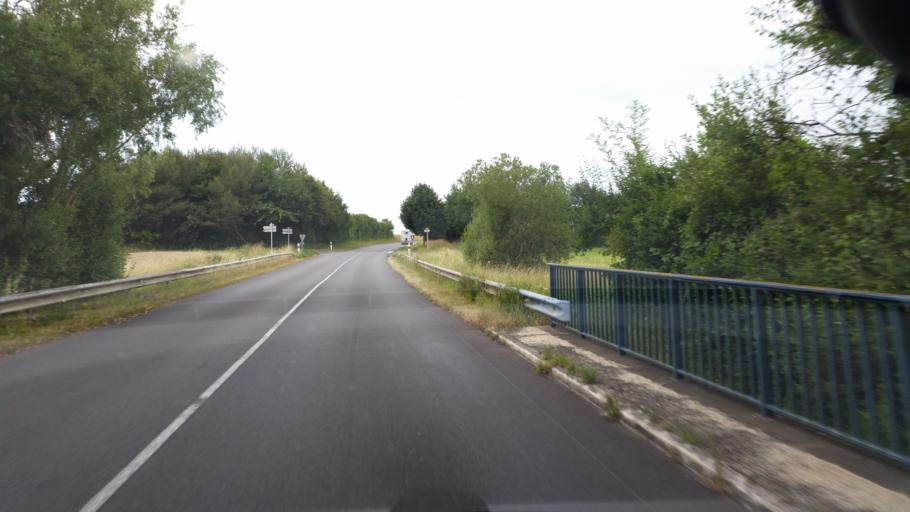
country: FR
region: Poitou-Charentes
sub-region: Departement de la Charente-Maritime
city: Surgeres
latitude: 46.1435
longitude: -0.8028
